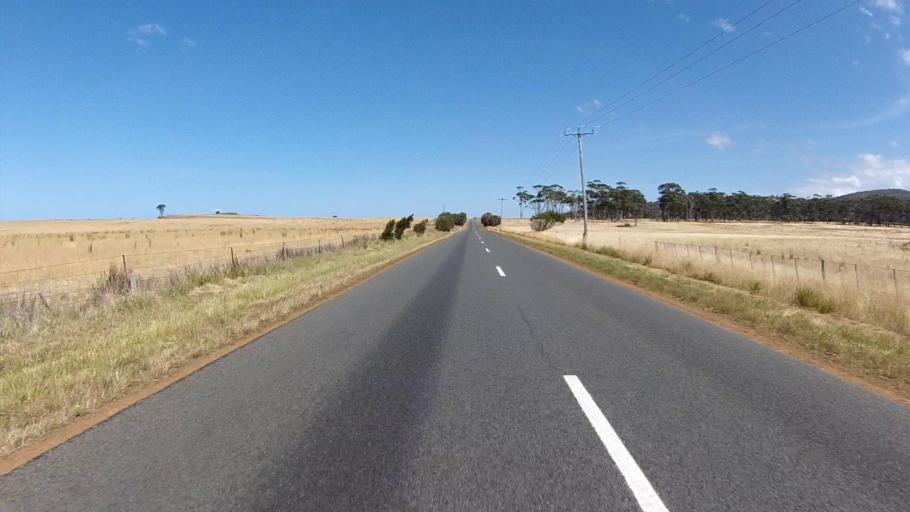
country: AU
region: Tasmania
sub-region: Sorell
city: Sorell
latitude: -42.2065
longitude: 148.0416
